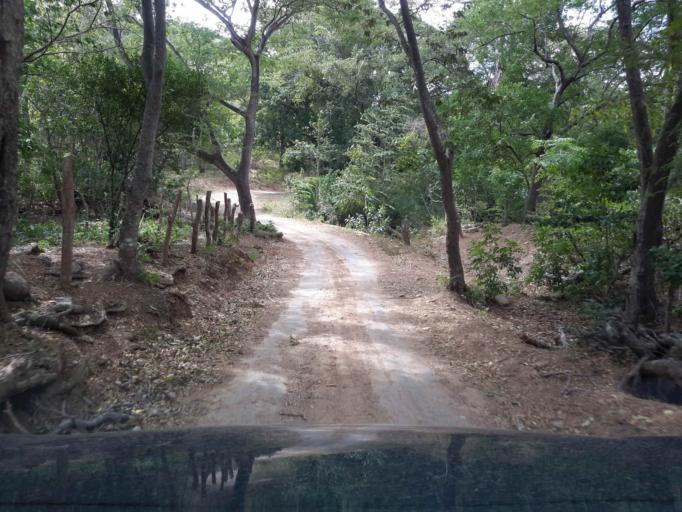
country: NI
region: Rivas
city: San Juan del Sur
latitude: 11.2269
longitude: -85.8257
